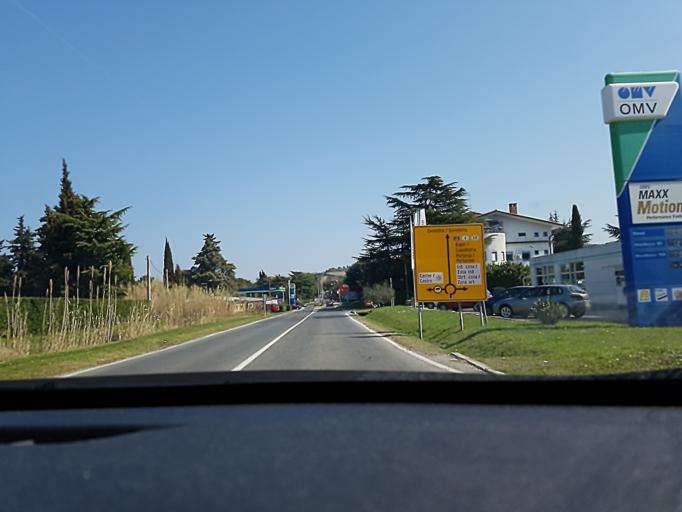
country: SI
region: Izola-Isola
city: Izola
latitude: 45.5369
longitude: 13.6675
